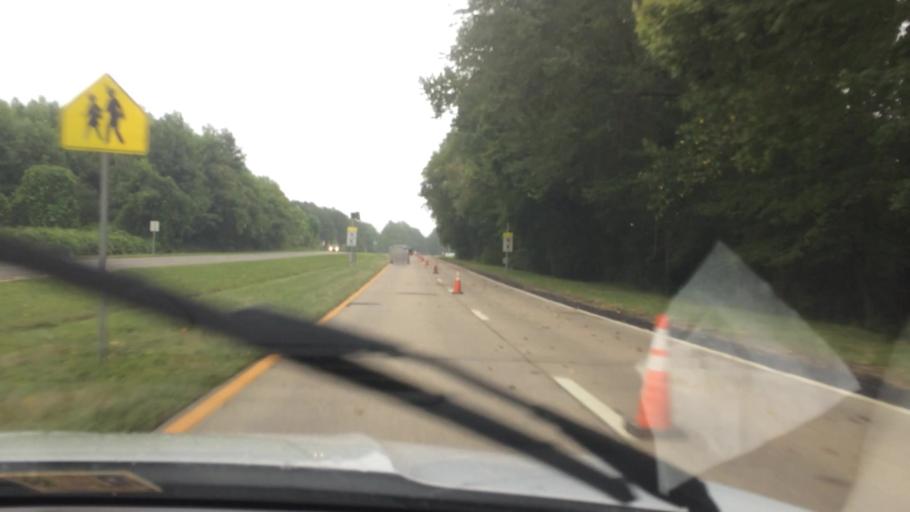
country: US
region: Virginia
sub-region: King William County
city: West Point
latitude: 37.3986
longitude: -76.7941
